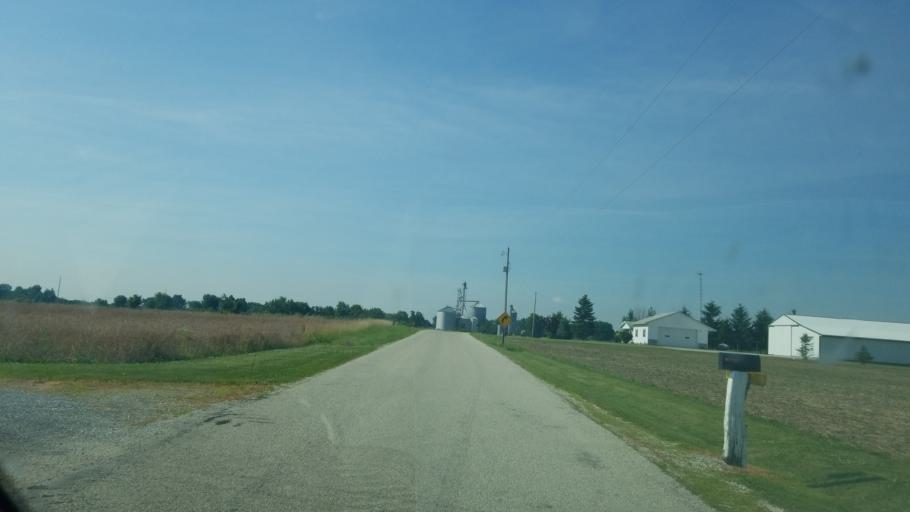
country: US
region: Ohio
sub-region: Wyandot County
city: Carey
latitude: 41.0077
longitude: -83.3244
